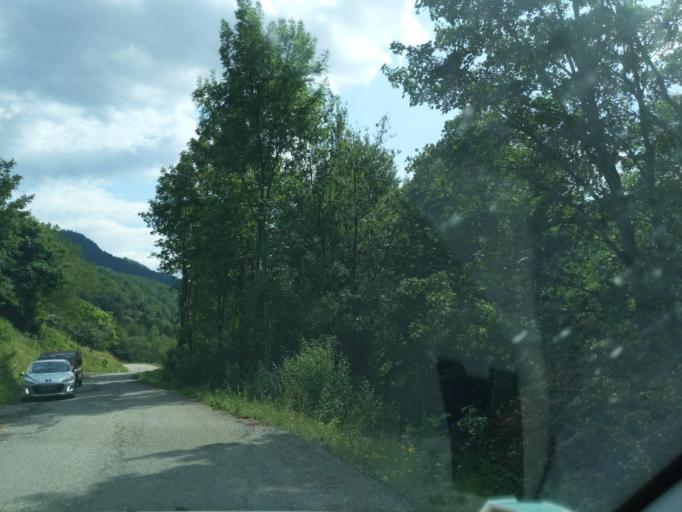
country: FR
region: Rhone-Alpes
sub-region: Departement de la Savoie
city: Ugine
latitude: 45.7379
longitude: 6.4341
